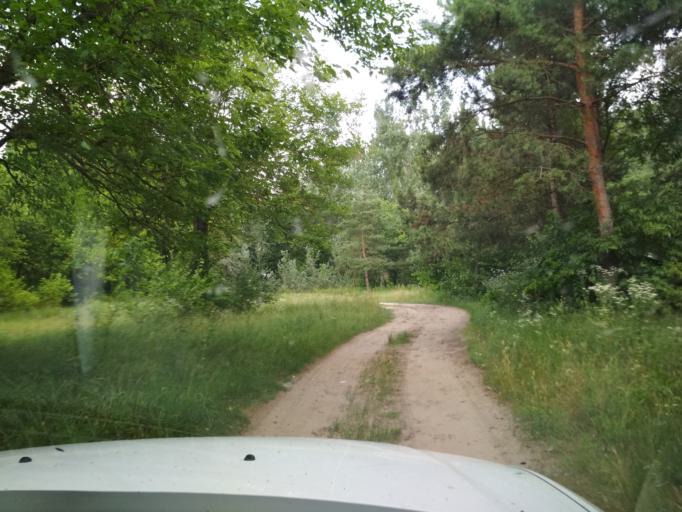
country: HU
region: Pest
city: Tapioszentmarton
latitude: 47.3301
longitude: 19.7625
